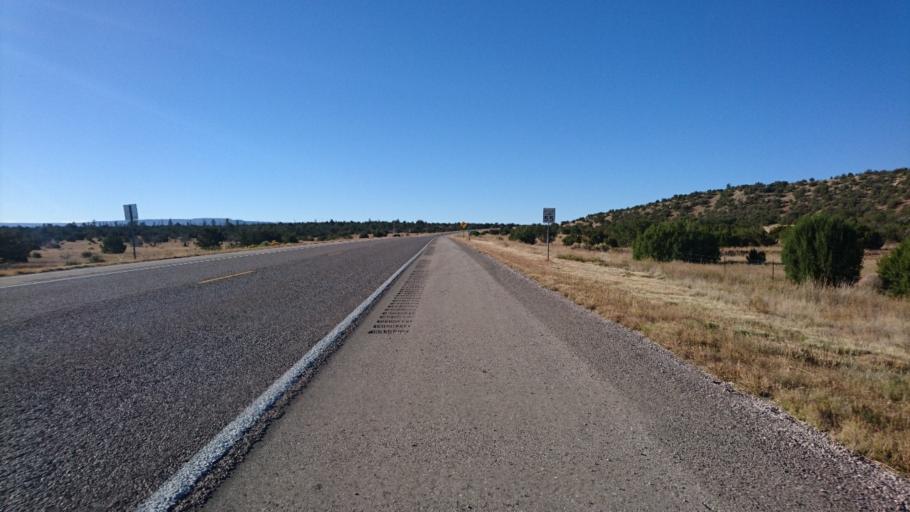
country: US
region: New Mexico
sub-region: Cibola County
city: Grants
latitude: 34.9692
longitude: -107.9127
